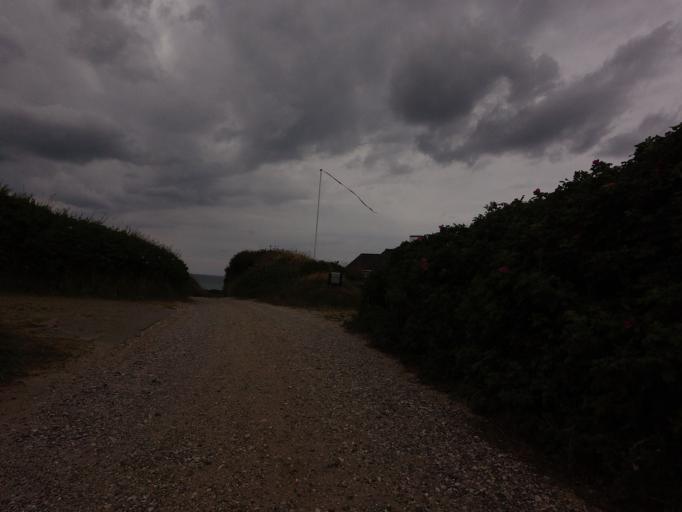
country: DK
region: North Denmark
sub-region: Jammerbugt Kommune
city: Pandrup
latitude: 57.3120
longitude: 9.6530
